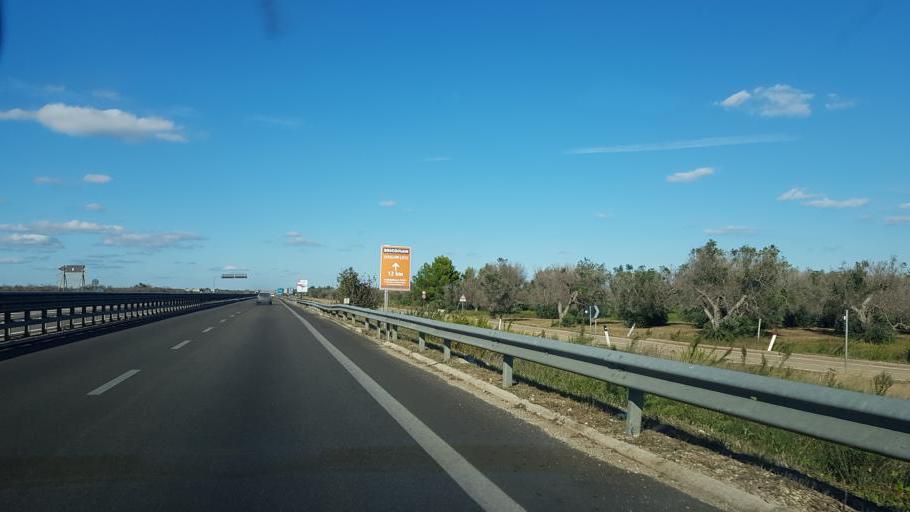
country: IT
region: Apulia
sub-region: Provincia di Lecce
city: San Pietro in Lama
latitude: 40.2581
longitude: 18.1189
